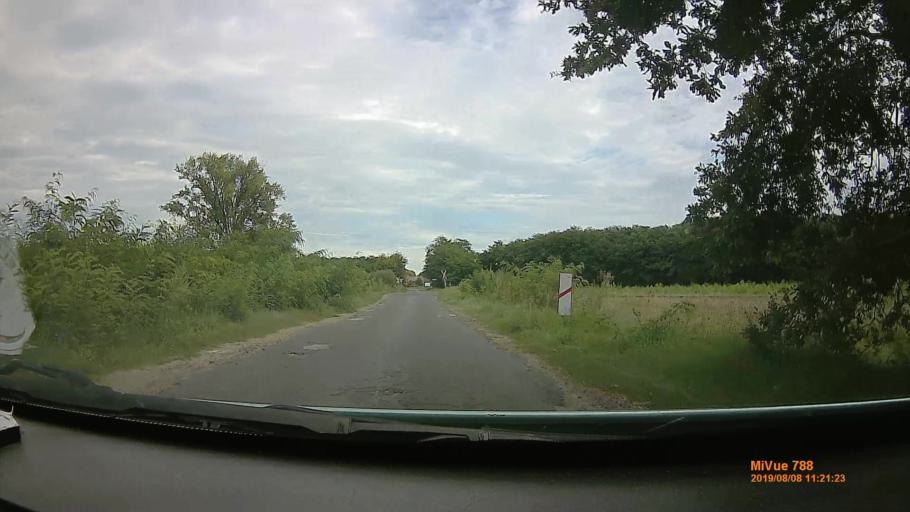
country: HU
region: Szabolcs-Szatmar-Bereg
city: Balkany
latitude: 47.7568
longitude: 21.8468
